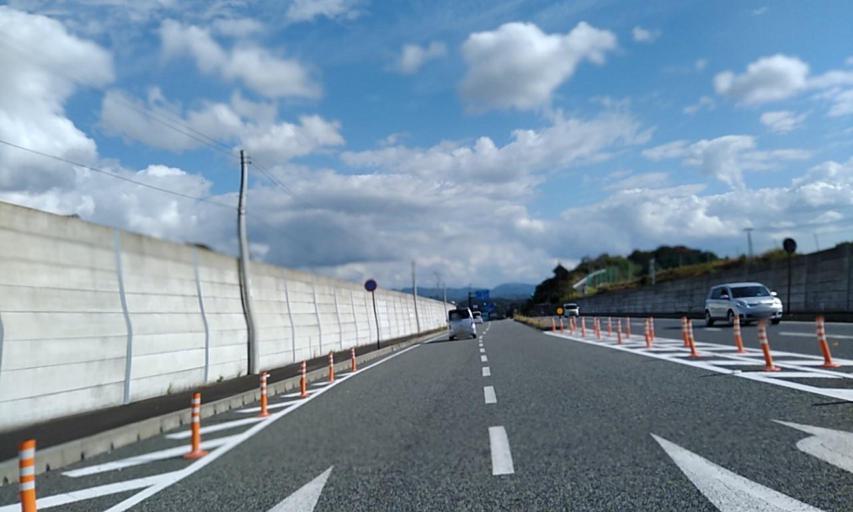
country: JP
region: Wakayama
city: Tanabe
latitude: 33.7478
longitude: 135.3643
